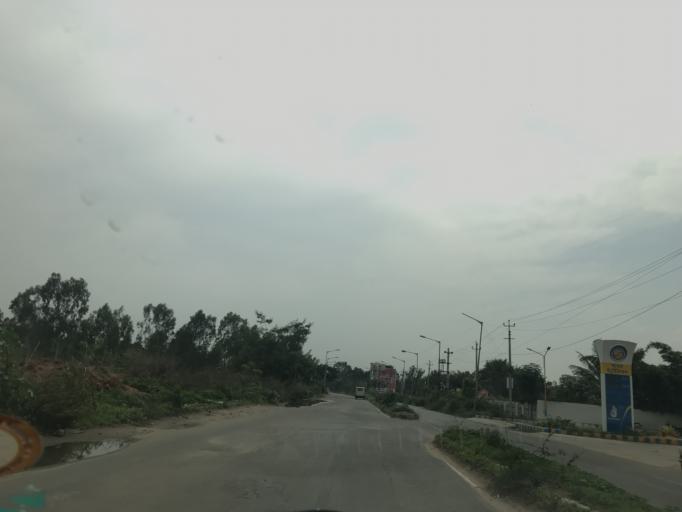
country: IN
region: Karnataka
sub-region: Bangalore Urban
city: Yelahanka
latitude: 13.1319
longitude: 77.6604
